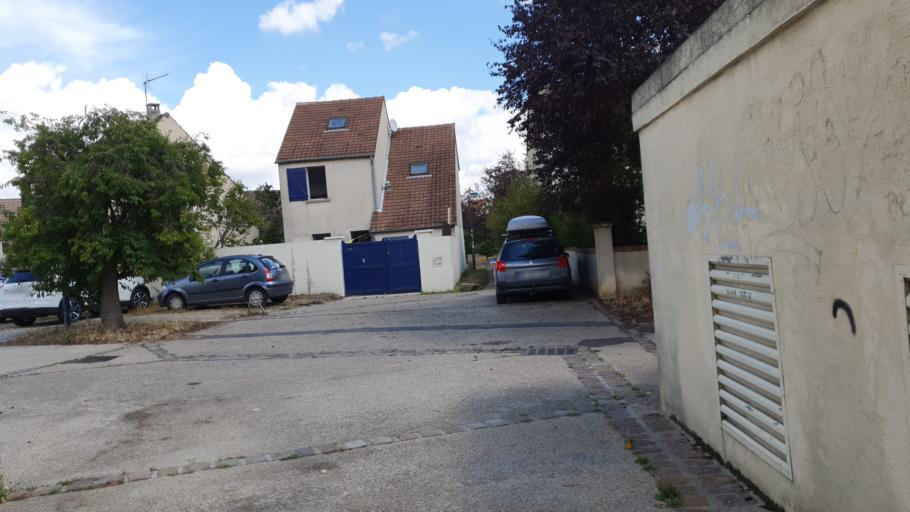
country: FR
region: Ile-de-France
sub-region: Departement des Yvelines
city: Conflans-Sainte-Honorine
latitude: 49.0059
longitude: 2.1028
